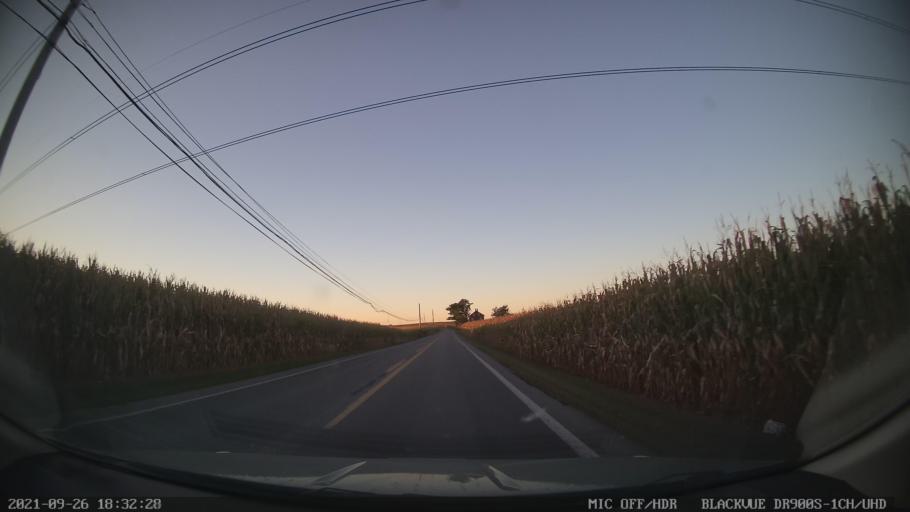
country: US
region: Pennsylvania
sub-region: Berks County
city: Kutztown
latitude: 40.4901
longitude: -75.7604
